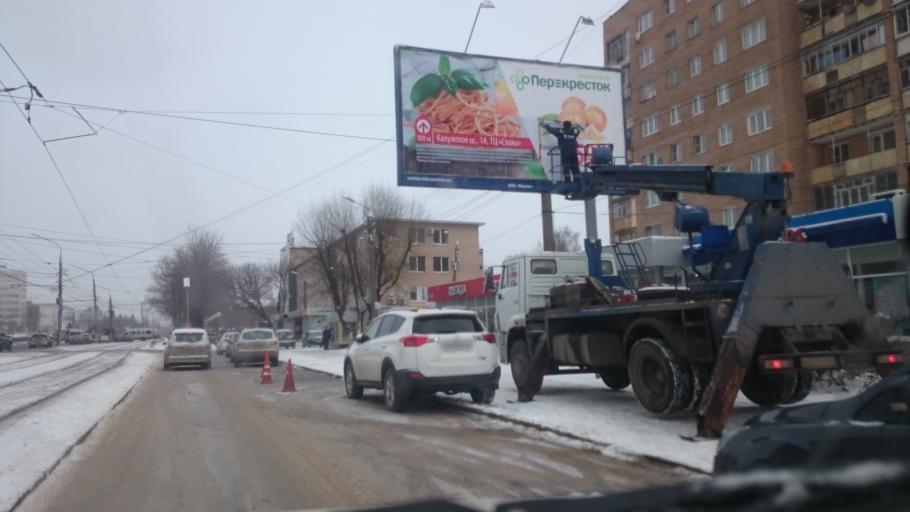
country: RU
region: Tula
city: Mendeleyevskiy
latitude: 54.1547
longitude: 37.5849
